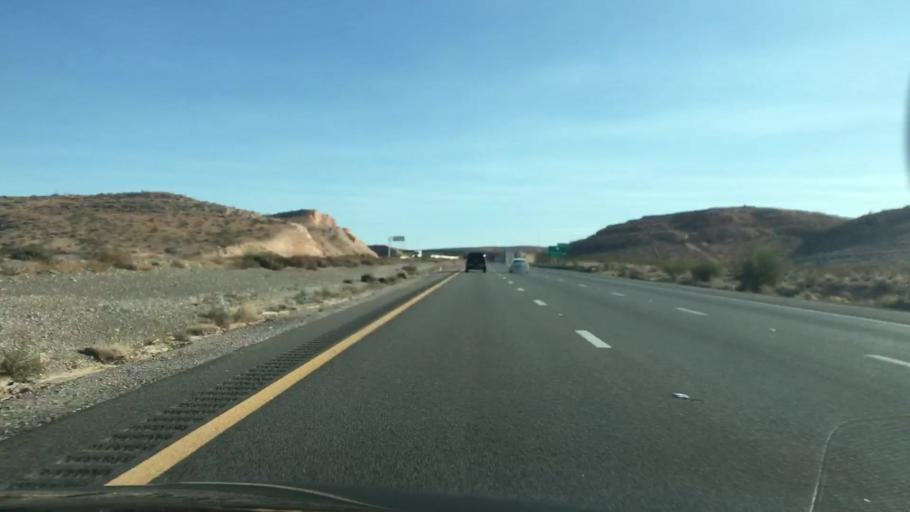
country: US
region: Nevada
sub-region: Clark County
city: Moapa Town
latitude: 36.6686
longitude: -114.5302
